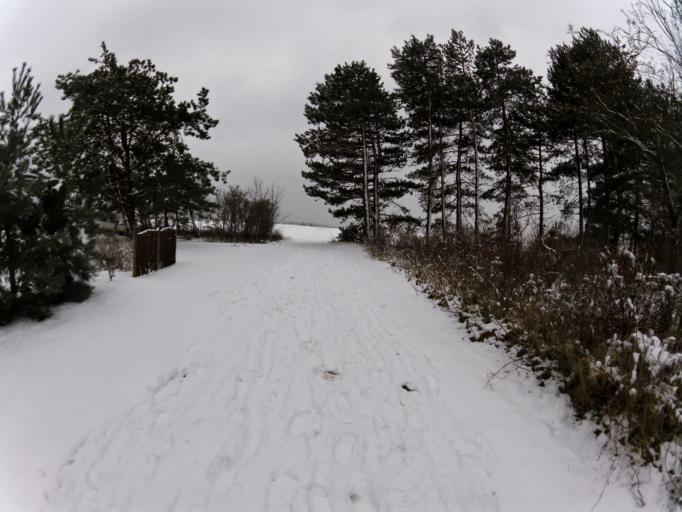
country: DK
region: Zealand
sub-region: Vordingborg Kommune
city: Neder Vindinge
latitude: 55.0513
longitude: 11.8326
